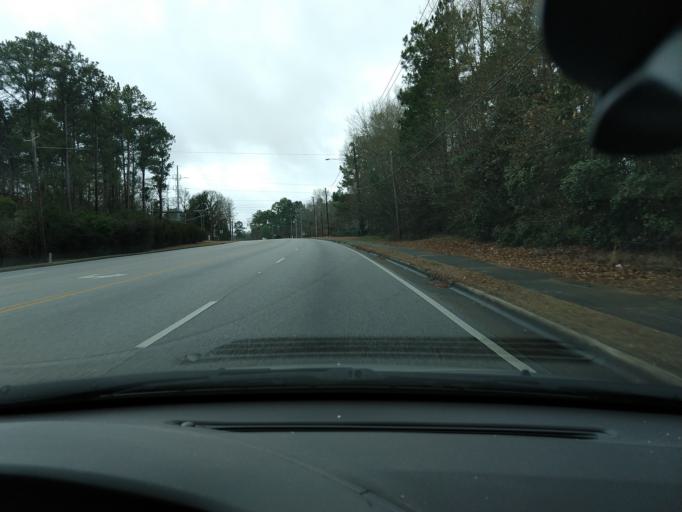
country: US
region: Alabama
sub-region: Houston County
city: Dothan
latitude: 31.2488
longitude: -85.4368
